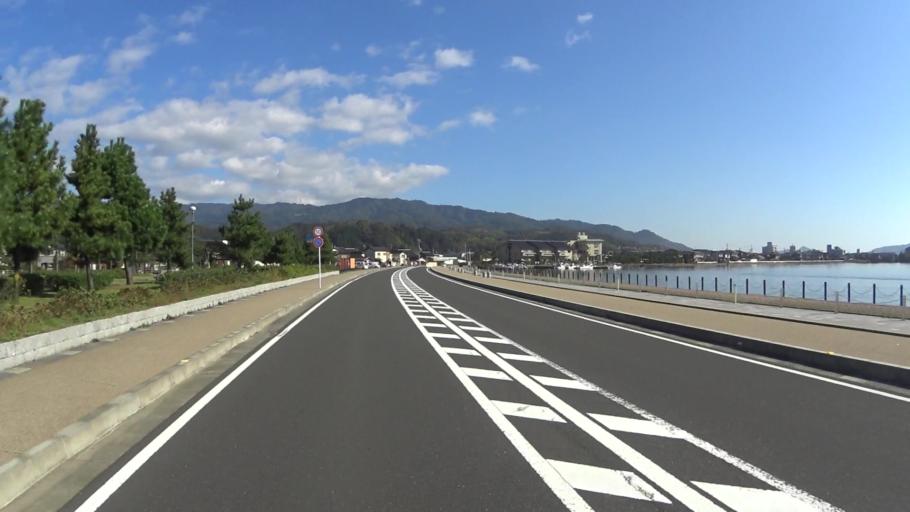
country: JP
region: Kyoto
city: Miyazu
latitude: 35.5672
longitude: 135.1564
